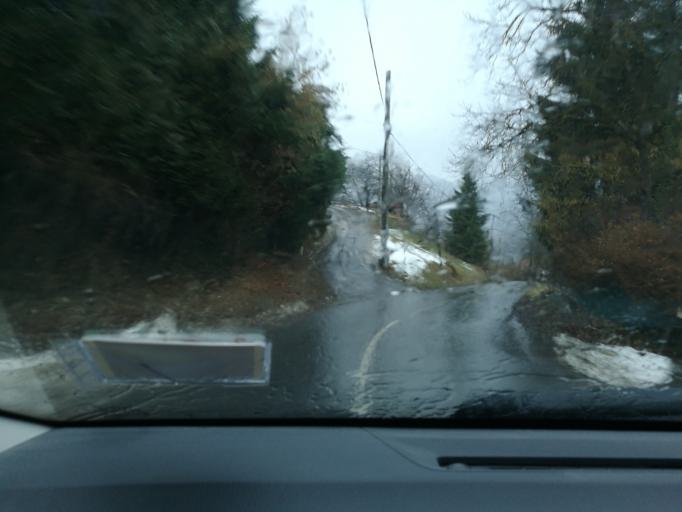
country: FR
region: Rhone-Alpes
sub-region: Departement de la Haute-Savoie
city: Saint-Gervais-les-Bains
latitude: 45.9001
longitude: 6.7005
